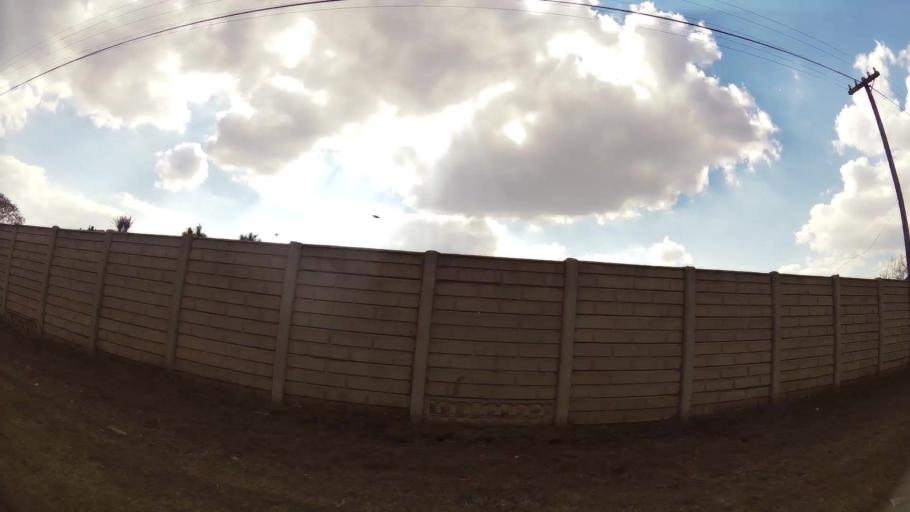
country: ZA
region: Mpumalanga
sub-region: Nkangala District Municipality
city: Delmas
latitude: -26.1307
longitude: 28.6742
